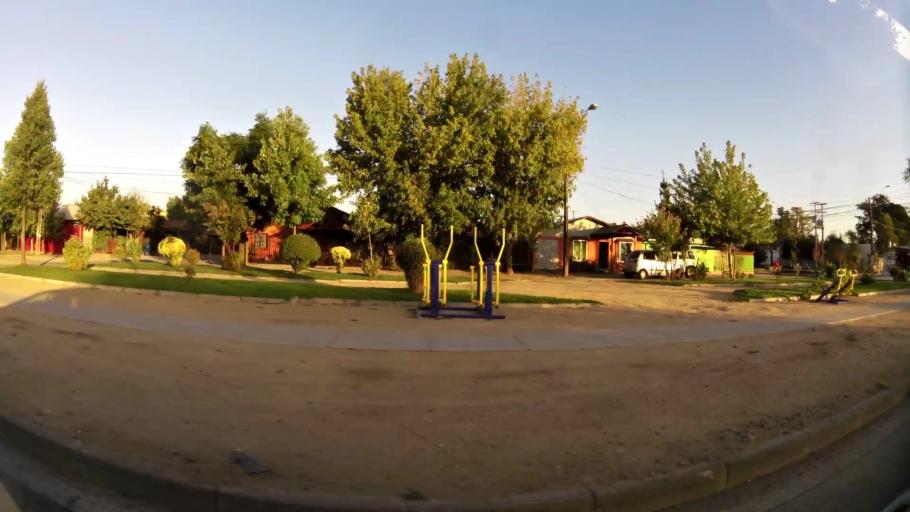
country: CL
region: Maule
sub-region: Provincia de Talca
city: Talca
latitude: -35.4466
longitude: -71.6550
